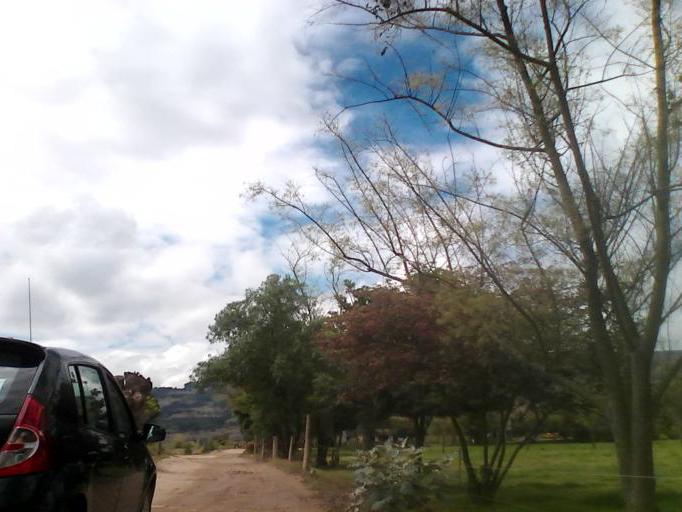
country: CO
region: Boyaca
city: Duitama
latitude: 5.7735
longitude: -73.0508
